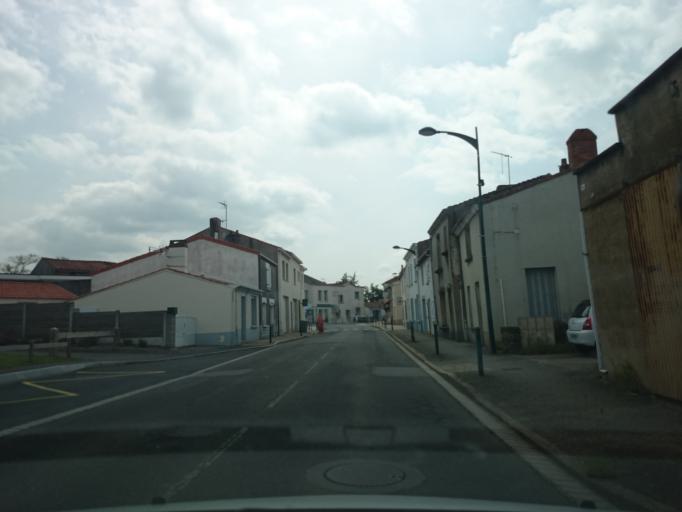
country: FR
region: Pays de la Loire
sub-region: Departement de la Loire-Atlantique
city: La Chevroliere
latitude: 47.0946
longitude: -1.6119
